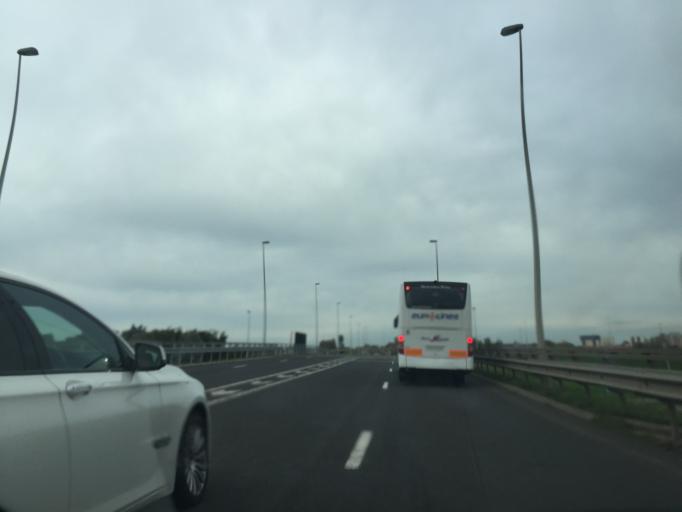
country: FR
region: Nord-Pas-de-Calais
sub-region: Departement du Pas-de-Calais
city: Coquelles
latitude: 50.9382
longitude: 1.8188
